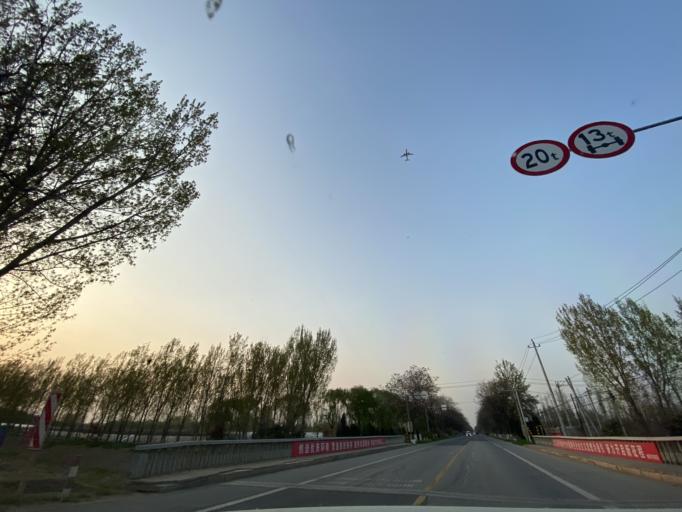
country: CN
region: Beijing
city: Weishanzhuang
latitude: 39.6063
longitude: 116.4096
